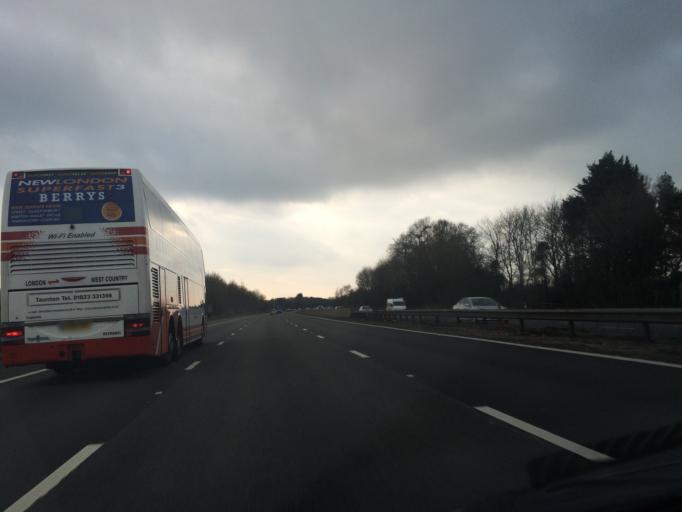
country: GB
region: England
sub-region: West Berkshire
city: Hungerford
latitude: 51.4563
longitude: -1.4930
